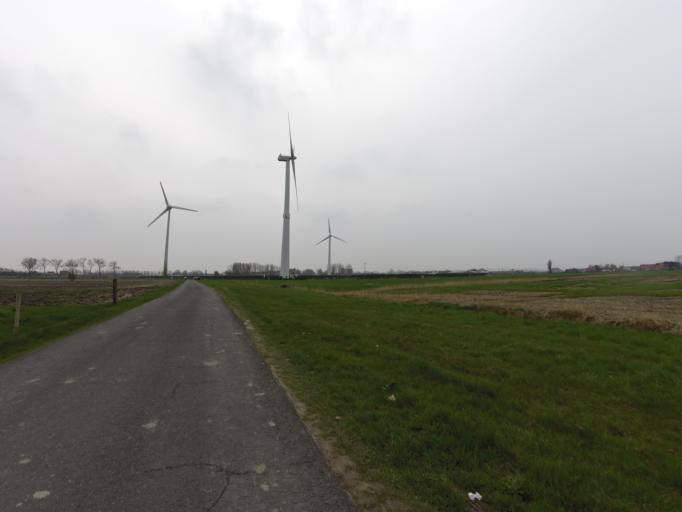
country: BE
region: Flanders
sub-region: Provincie West-Vlaanderen
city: Nieuwpoort
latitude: 51.1425
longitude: 2.7650
